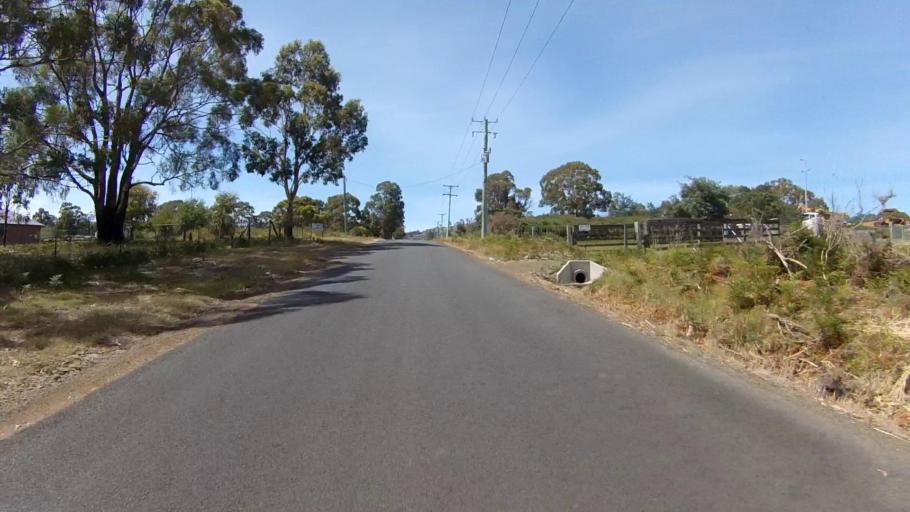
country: AU
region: Tasmania
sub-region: Sorell
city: Sorell
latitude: -42.6132
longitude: 147.7267
